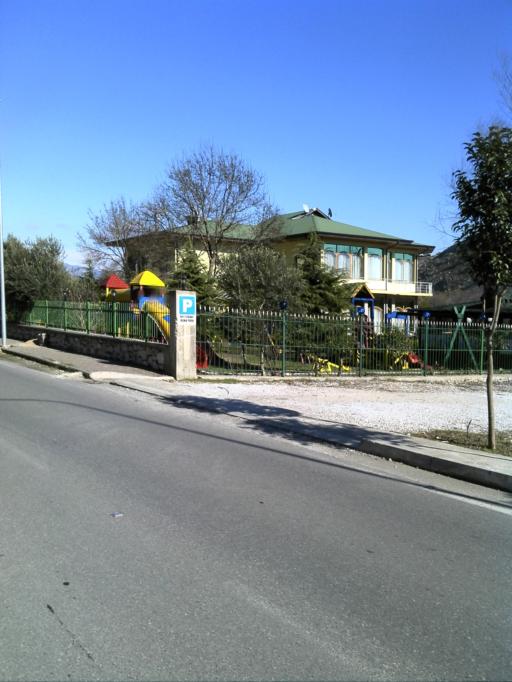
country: AL
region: Shkoder
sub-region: Rrethi i Shkodres
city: Berdica e Madhe
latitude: 42.0469
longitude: 19.4862
